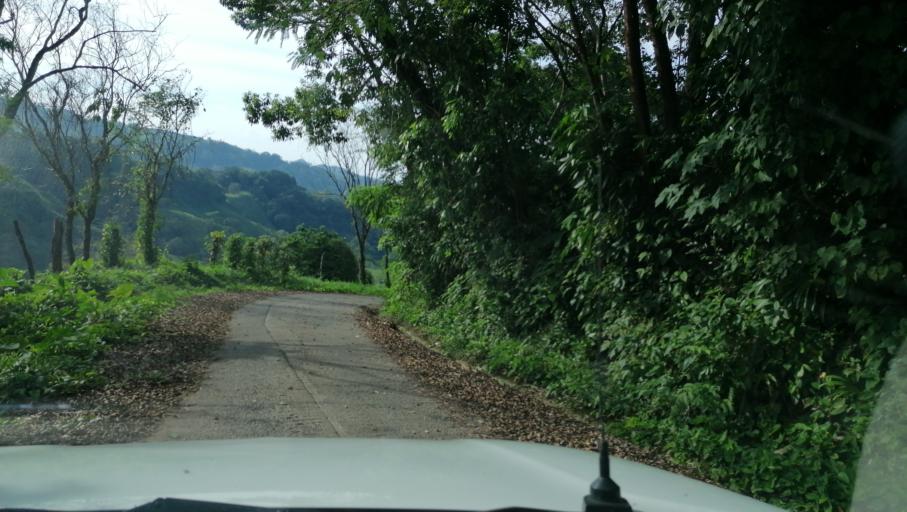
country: MX
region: Chiapas
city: Ostuacan
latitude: 17.4688
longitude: -93.2344
